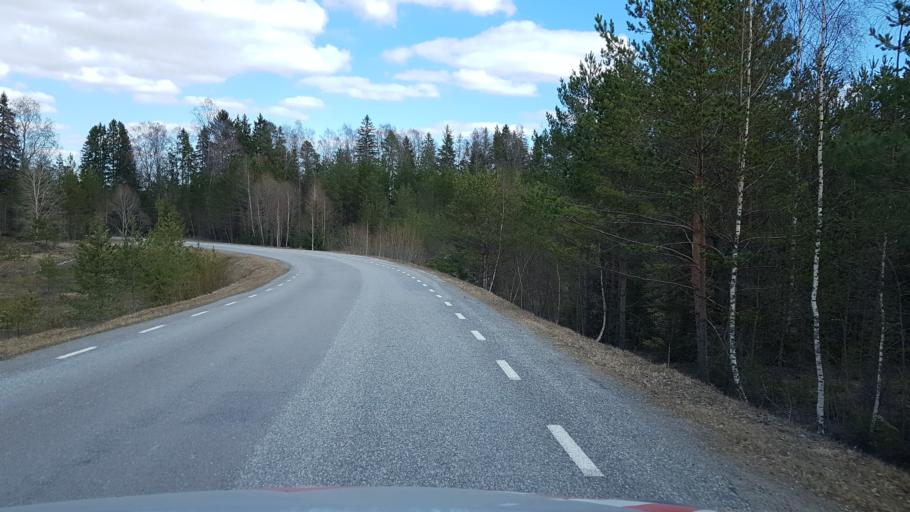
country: EE
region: Laeaene-Virumaa
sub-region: Kadrina vald
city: Kadrina
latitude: 59.2407
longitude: 26.1830
